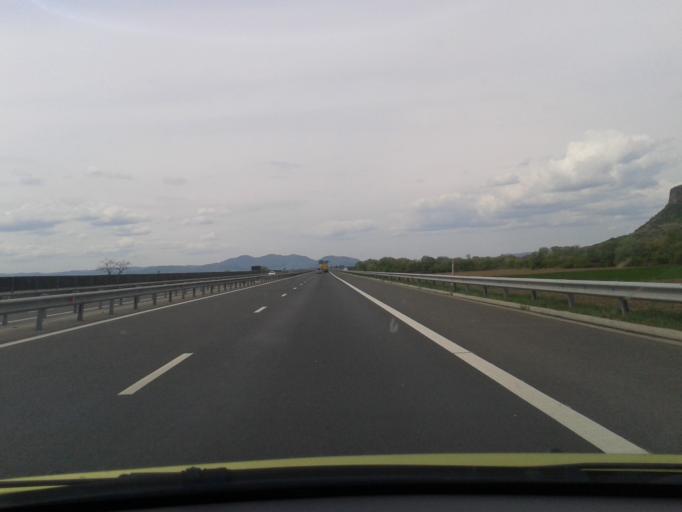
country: RO
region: Hunedoara
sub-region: Comuna Rapoltu Mare
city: Rapoltu Mare
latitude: 45.8463
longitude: 23.0620
